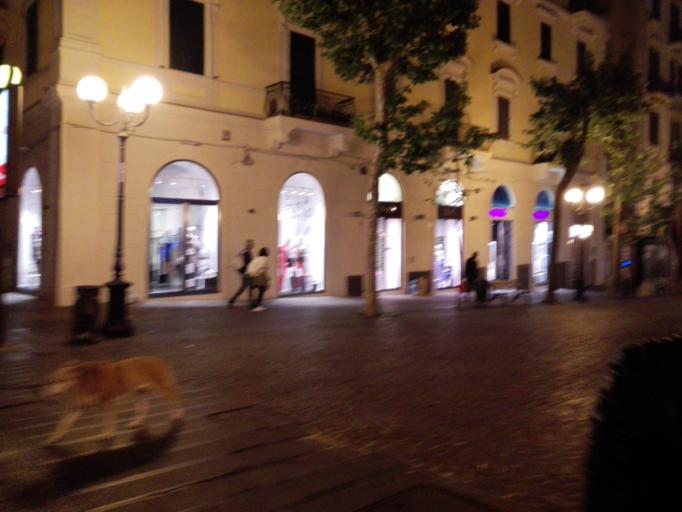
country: IT
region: Campania
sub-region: Provincia di Napoli
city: Napoli
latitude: 40.8436
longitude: 14.2292
